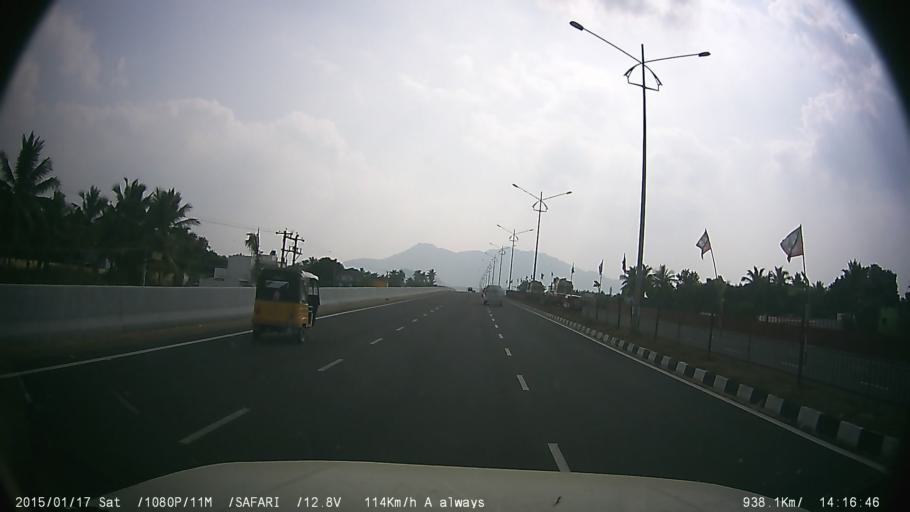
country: IN
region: Tamil Nadu
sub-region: Vellore
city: Ambur
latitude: 12.7493
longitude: 78.6974
